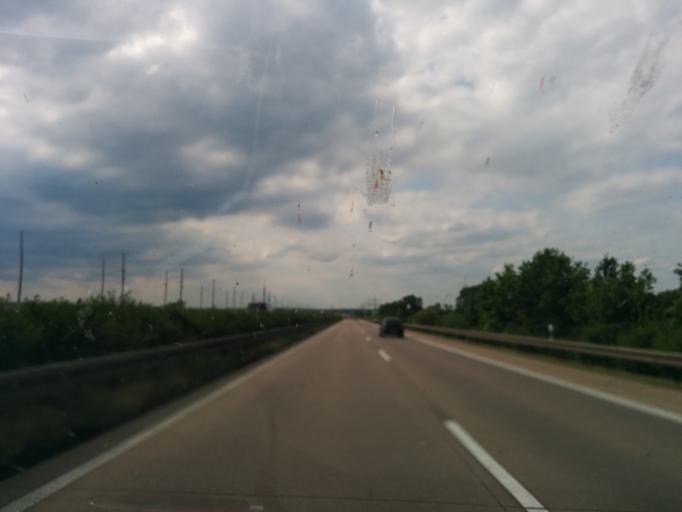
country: DE
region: Thuringia
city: Ichtershausen
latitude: 50.8708
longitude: 10.9947
